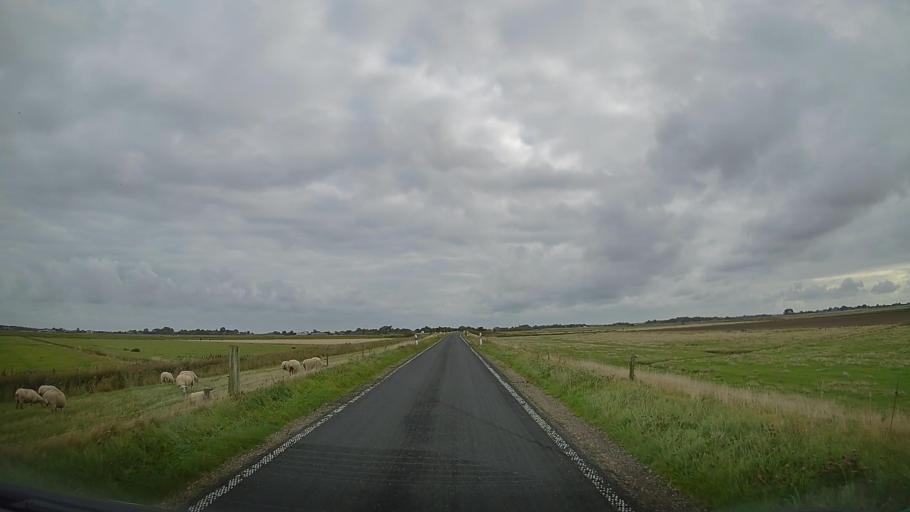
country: DE
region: Schleswig-Holstein
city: Neukirchen
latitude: 54.8926
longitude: 8.7289
